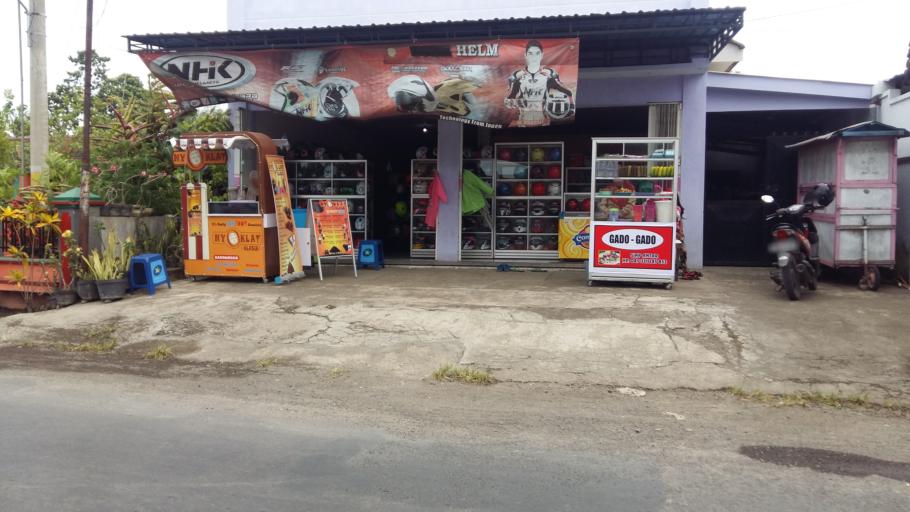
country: ID
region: East Java
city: Krajan
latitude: -8.3110
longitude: 114.2938
